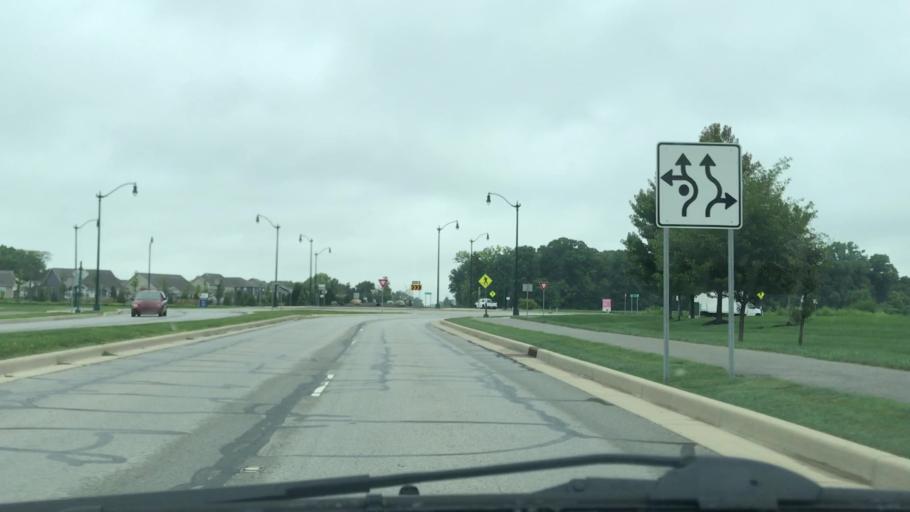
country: US
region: Indiana
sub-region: Hamilton County
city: Westfield
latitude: 40.0212
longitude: -86.0706
